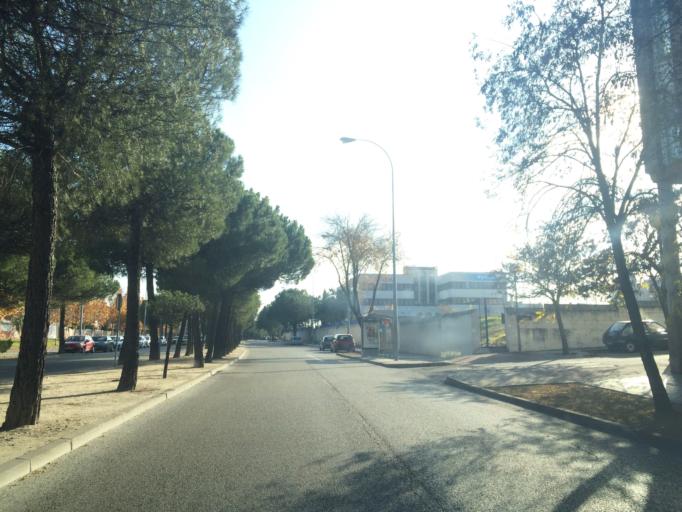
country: ES
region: Madrid
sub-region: Provincia de Madrid
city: Tres Cantos
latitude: 40.5951
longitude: -3.7068
